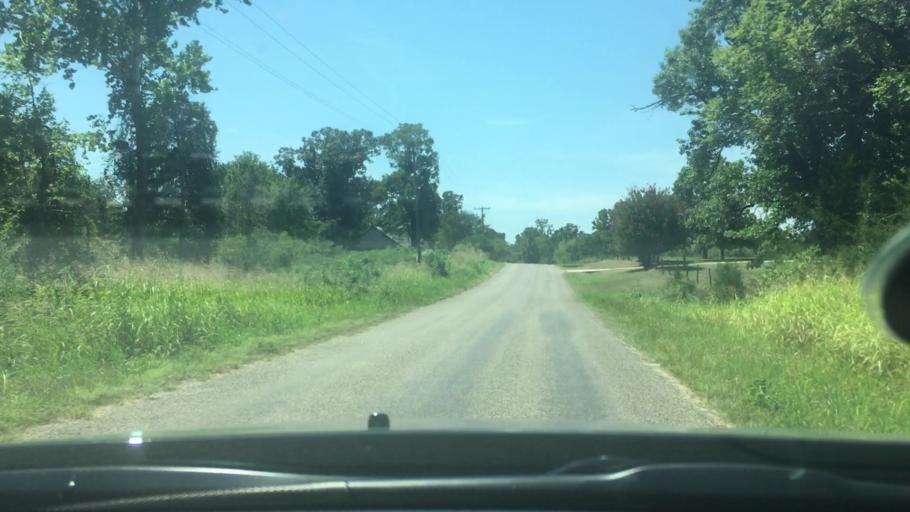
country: US
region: Oklahoma
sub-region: Bryan County
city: Durant
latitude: 33.9806
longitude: -96.2511
